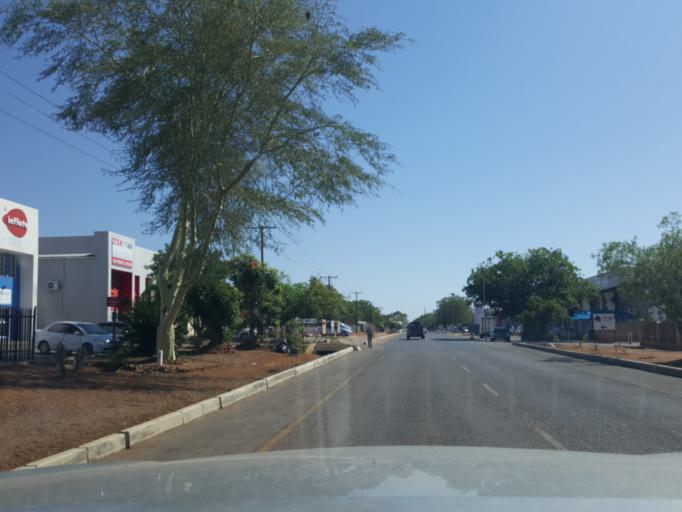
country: BW
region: South East
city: Gaborone
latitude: -24.6929
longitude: 25.8810
